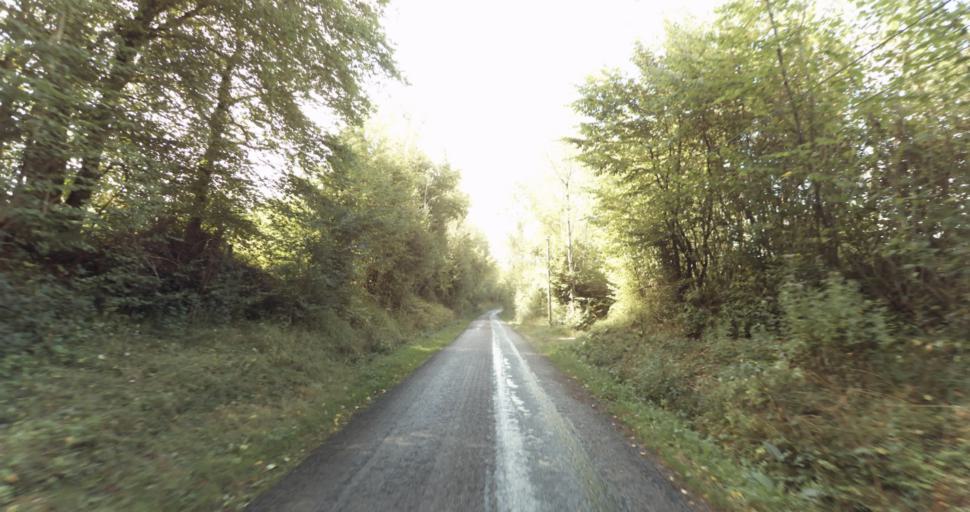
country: FR
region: Lower Normandy
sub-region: Departement de l'Orne
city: Gace
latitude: 48.7868
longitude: 0.3122
